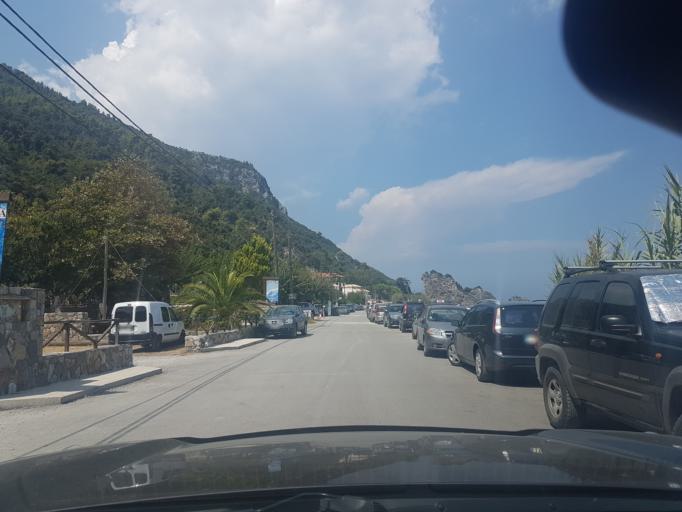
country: GR
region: Central Greece
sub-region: Nomos Evvoias
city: Kymi
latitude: 38.6696
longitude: 23.9230
